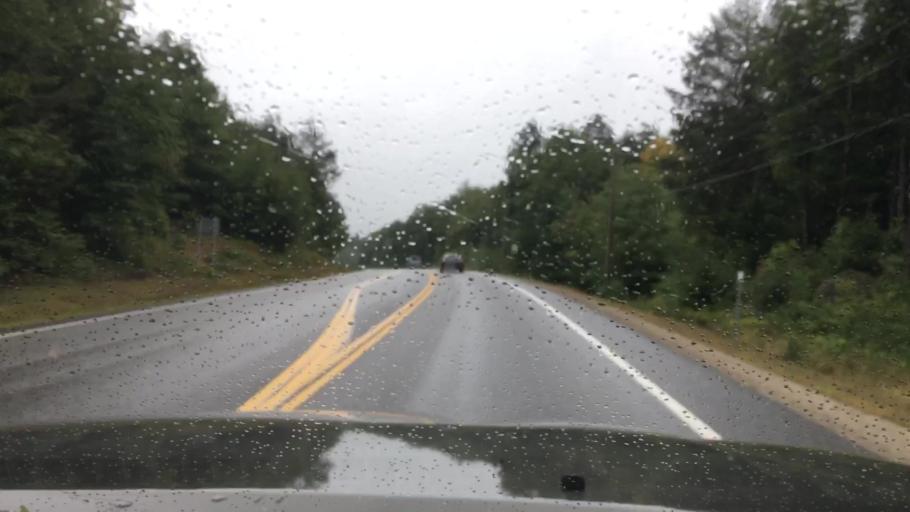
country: US
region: New Hampshire
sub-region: Cheshire County
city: Harrisville
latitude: 43.0556
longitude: -72.0780
